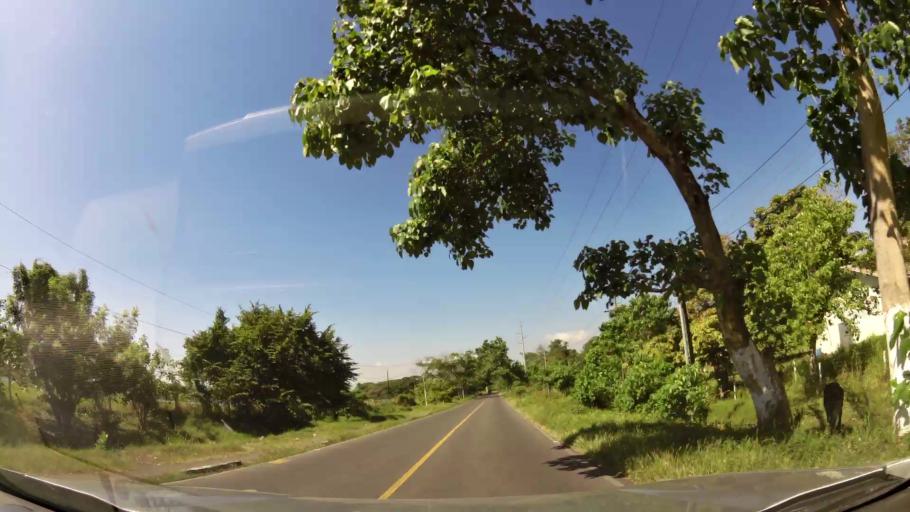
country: GT
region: Escuintla
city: Iztapa
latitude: 13.9368
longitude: -90.7400
